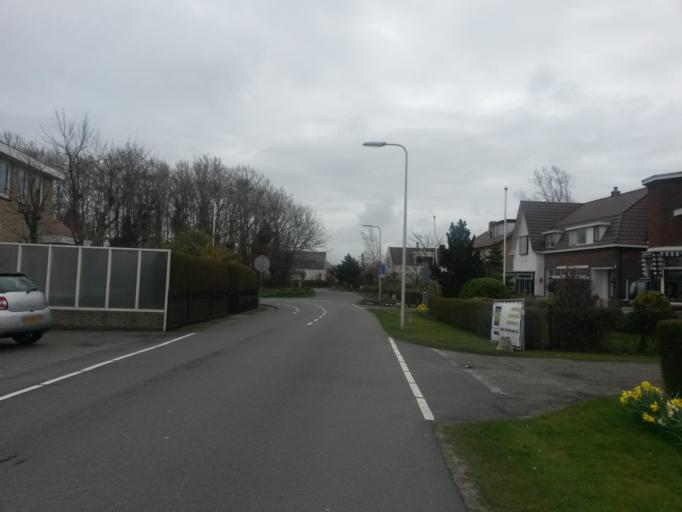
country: NL
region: South Holland
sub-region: Gemeente Rotterdam
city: Hoek van Holland
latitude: 52.0001
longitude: 4.1406
